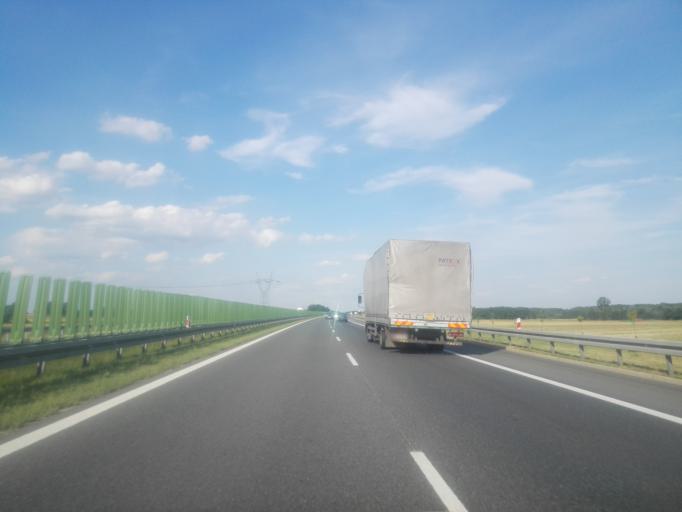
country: PL
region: Lower Silesian Voivodeship
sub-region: Powiat wroclawski
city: Dlugoleka
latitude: 51.2199
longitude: 17.1457
